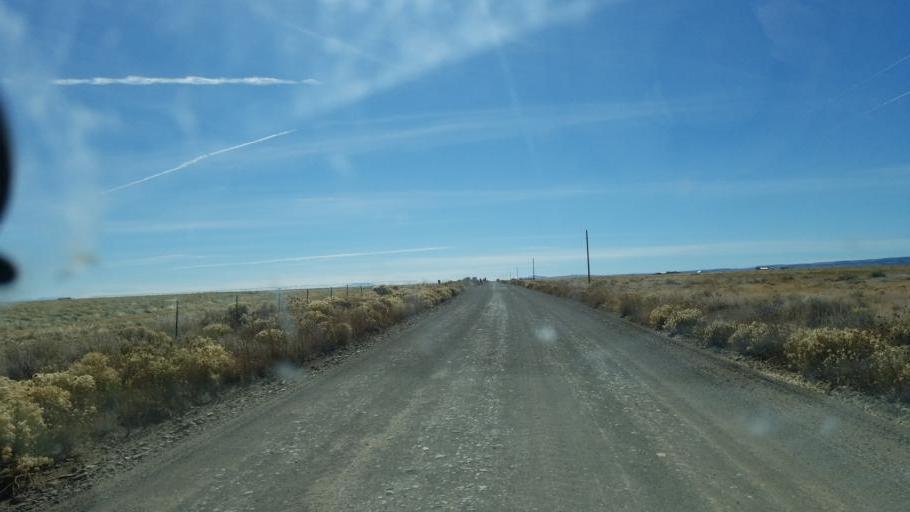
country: US
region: Colorado
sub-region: Rio Grande County
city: Monte Vista
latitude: 37.3962
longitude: -106.1495
